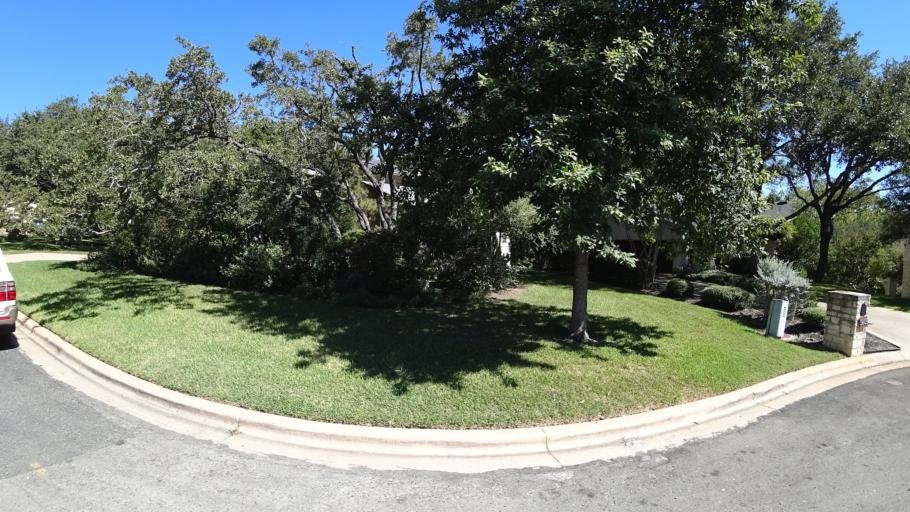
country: US
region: Texas
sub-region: Travis County
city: West Lake Hills
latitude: 30.3401
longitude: -97.7835
